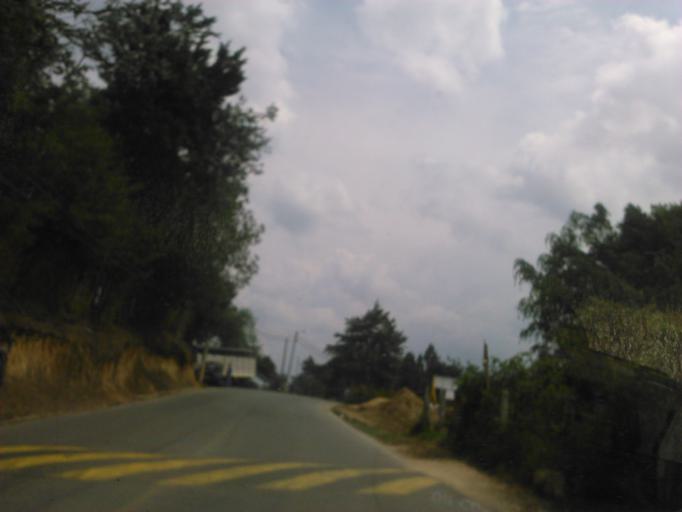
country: CO
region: Antioquia
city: San Vicente
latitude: 6.2325
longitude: -75.3861
